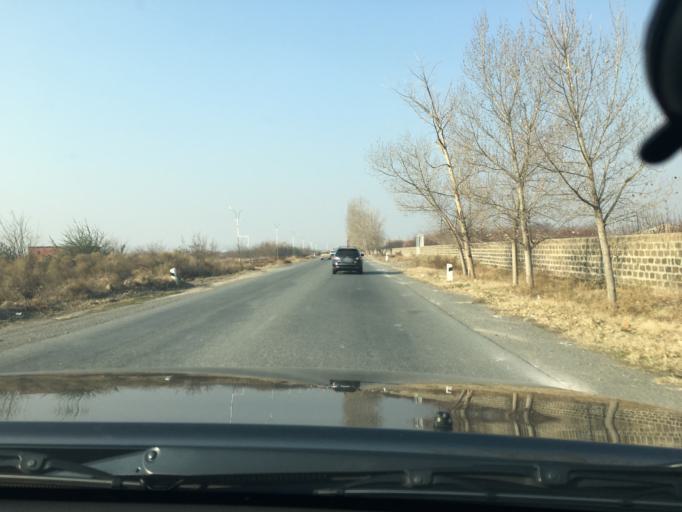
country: AM
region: Armavir
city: Myasnikyan
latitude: 40.1758
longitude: 43.9445
